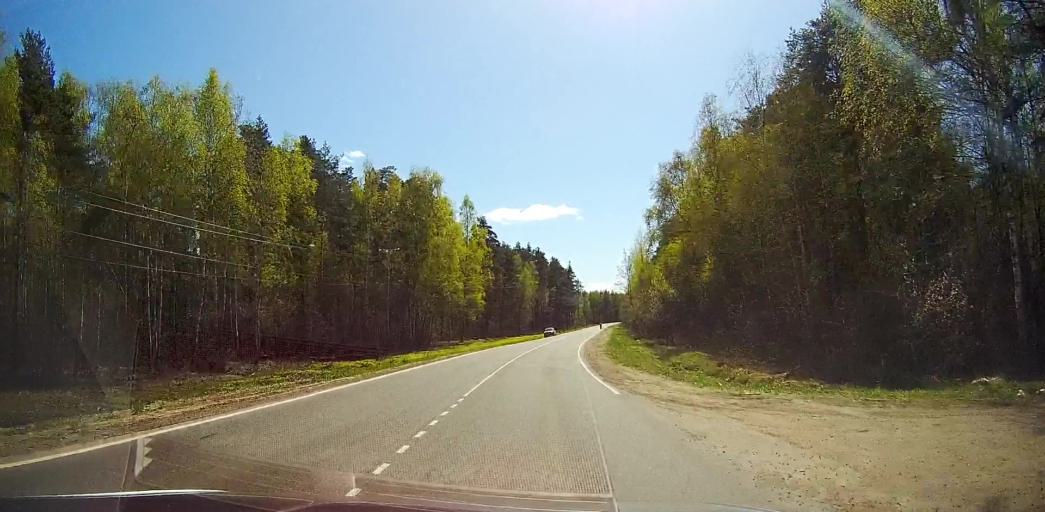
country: RU
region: Moskovskaya
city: Beloozerskiy
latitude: 55.5013
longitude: 38.4311
